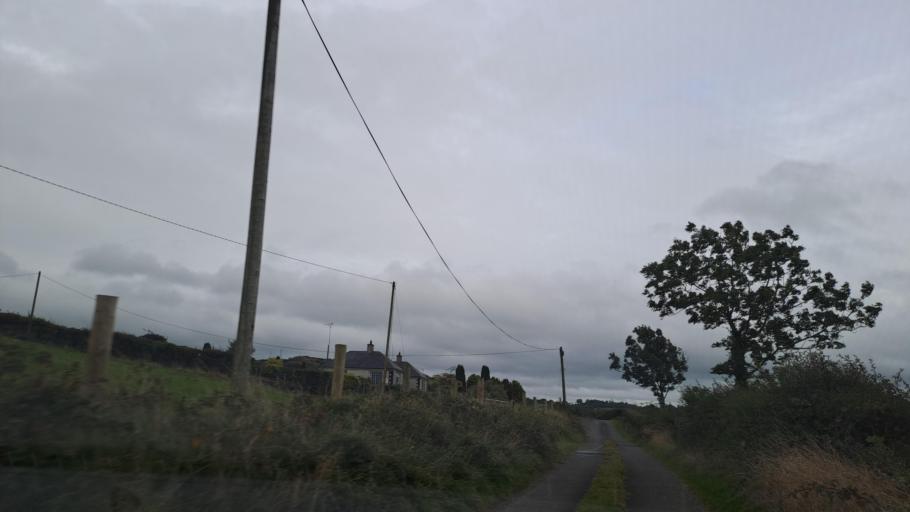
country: IE
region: Ulster
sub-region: An Cabhan
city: Bailieborough
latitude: 53.9802
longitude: -6.9093
